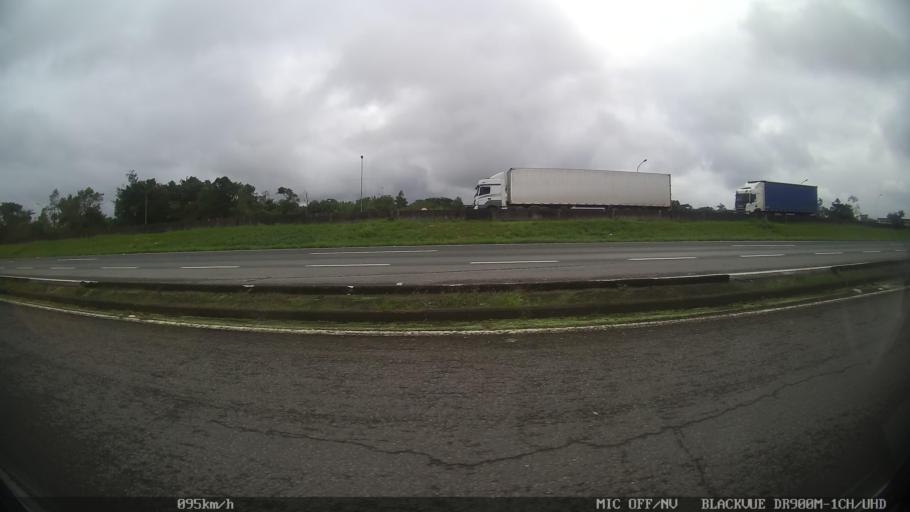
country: BR
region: Sao Paulo
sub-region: Registro
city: Registro
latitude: -24.5358
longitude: -47.8582
